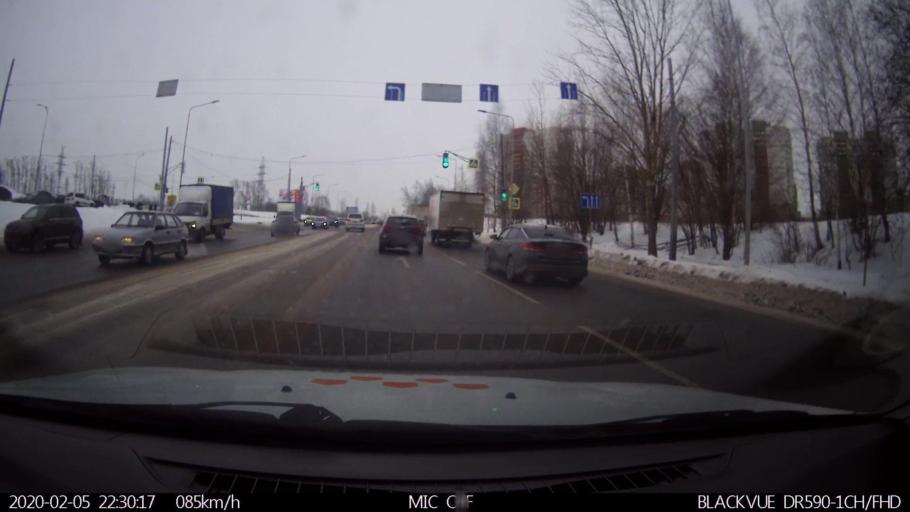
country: RU
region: Nizjnij Novgorod
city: Imeni Stepana Razina
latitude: 54.7438
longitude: 44.1582
